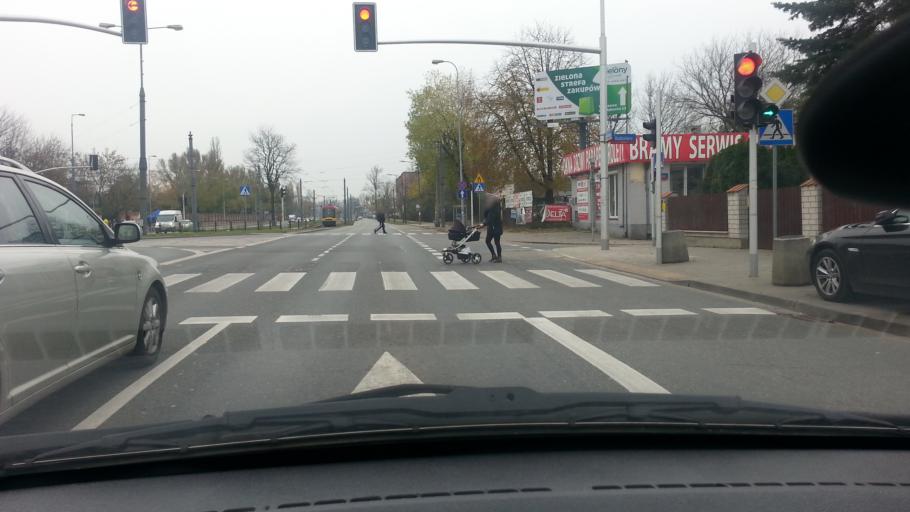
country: PL
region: Masovian Voivodeship
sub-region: Warszawa
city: Targowek
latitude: 52.2812
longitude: 21.0254
